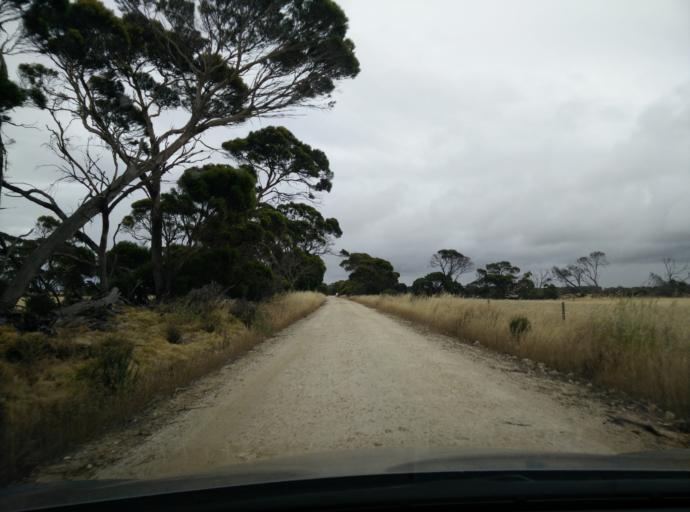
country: AU
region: South Australia
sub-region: Kangaroo Island
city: Kingscote
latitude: -35.8689
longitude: 137.5286
